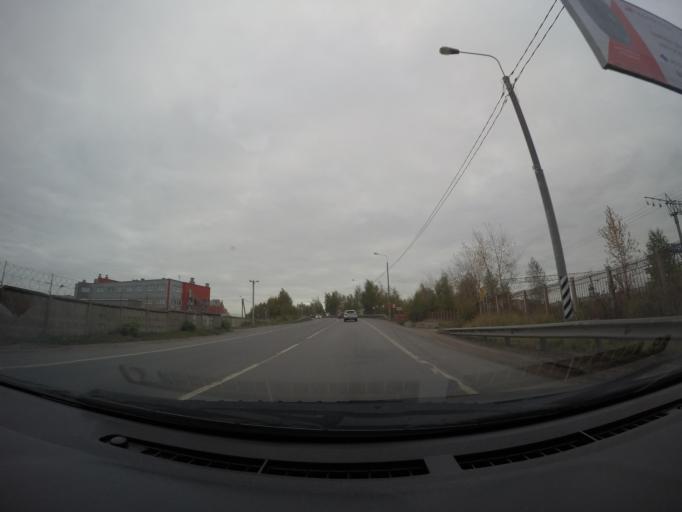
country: RU
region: Moskovskaya
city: Elektrougli
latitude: 55.7261
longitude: 38.2178
